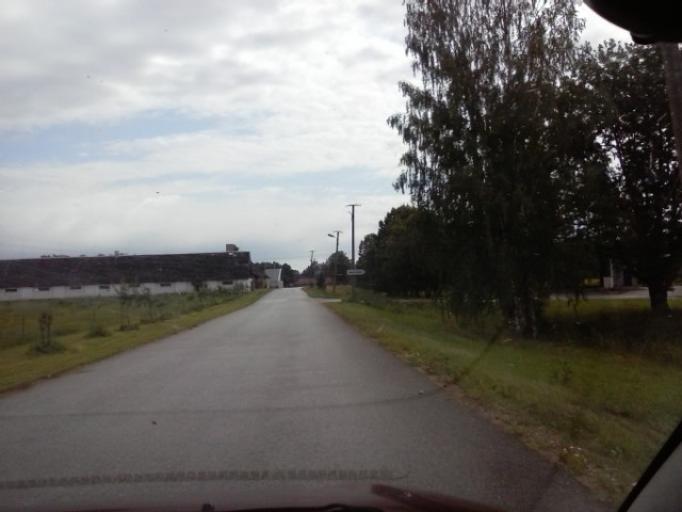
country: EE
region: Tartu
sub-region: Tartu linn
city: Tartu
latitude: 58.3605
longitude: 26.8772
